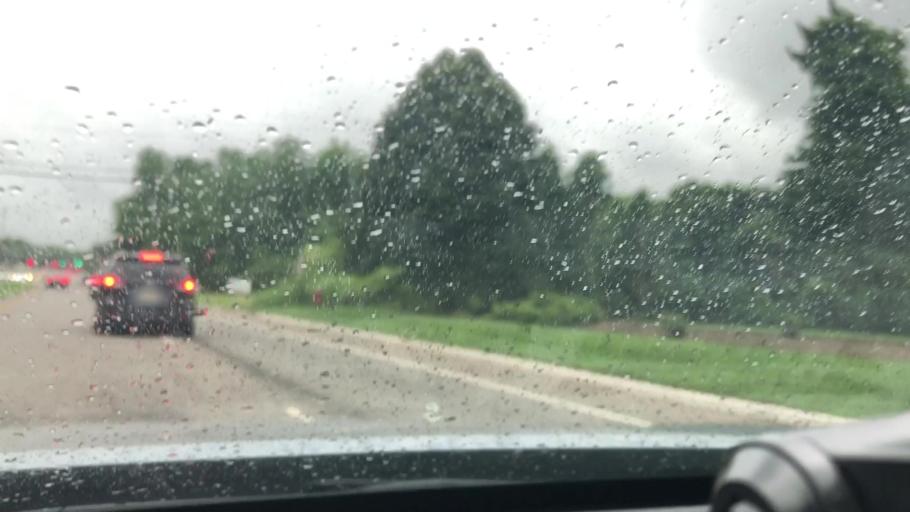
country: US
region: New Jersey
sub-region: Morris County
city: Hanover
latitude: 40.8015
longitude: -74.3413
